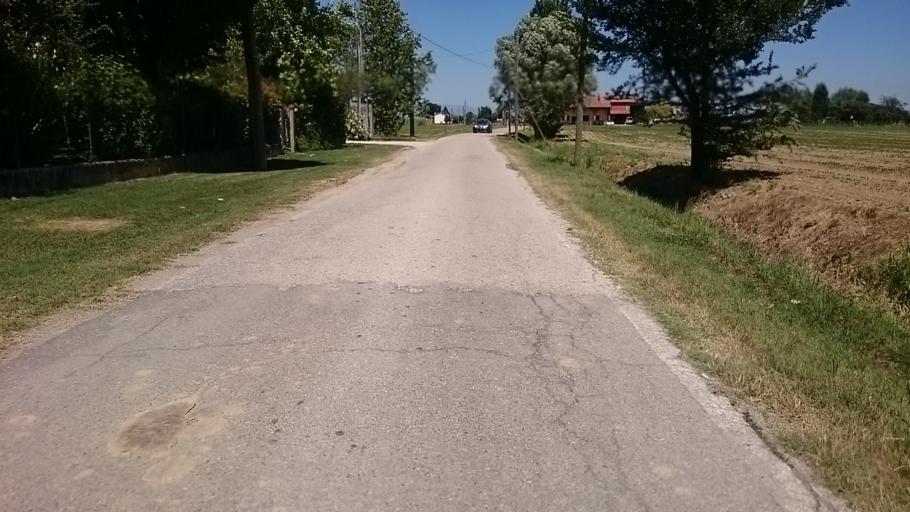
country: IT
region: Veneto
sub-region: Provincia di Padova
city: Borgoricco-San Michele delle Badesse-Sant'Eufemia
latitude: 45.5295
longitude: 11.9285
